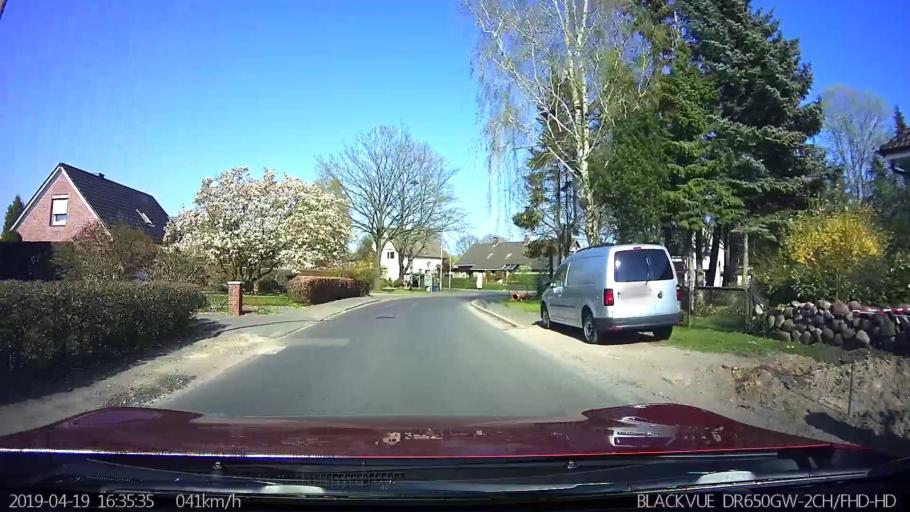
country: DE
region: Schleswig-Holstein
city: Tangstedt
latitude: 53.6694
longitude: 9.8400
